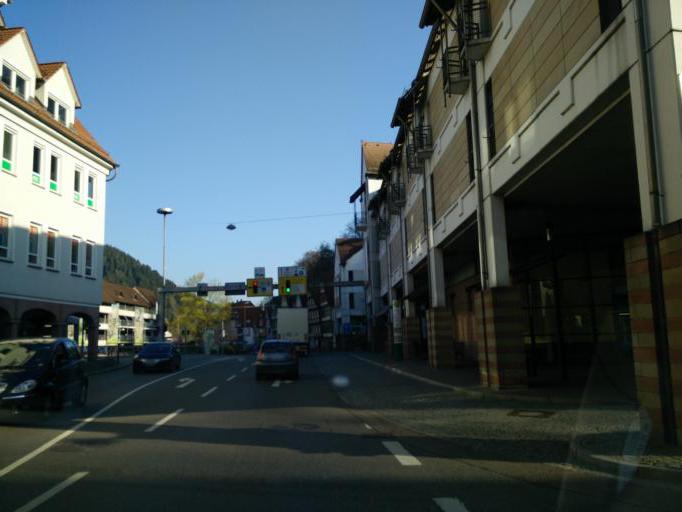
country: DE
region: Baden-Wuerttemberg
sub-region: Karlsruhe Region
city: Calw
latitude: 48.7140
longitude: 8.7415
